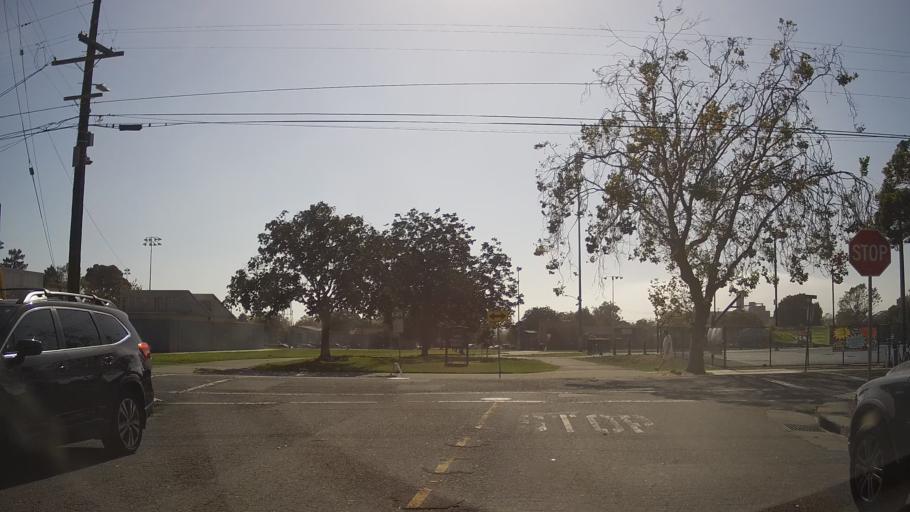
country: US
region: California
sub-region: Alameda County
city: Berkeley
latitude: 37.8557
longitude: -122.2827
